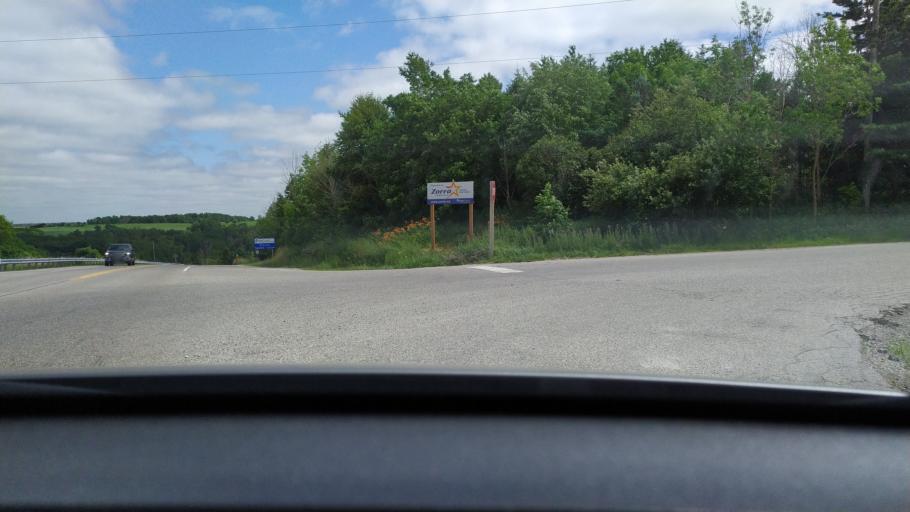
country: CA
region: Ontario
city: Stratford
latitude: 43.2822
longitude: -80.9647
